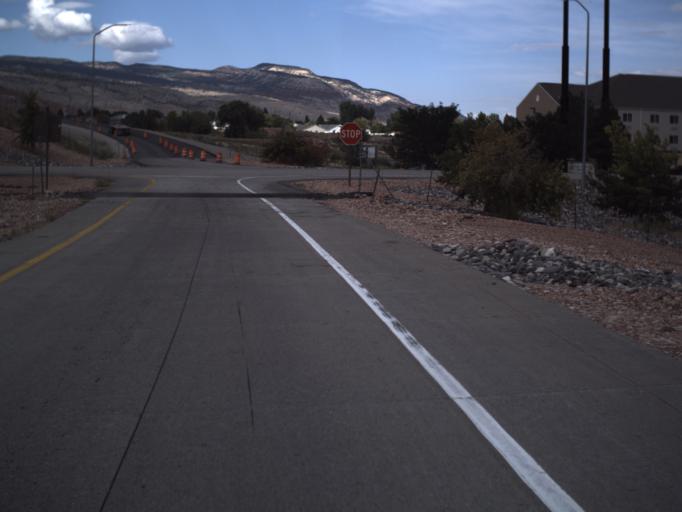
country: US
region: Utah
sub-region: Sevier County
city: Richfield
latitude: 38.7493
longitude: -112.1054
